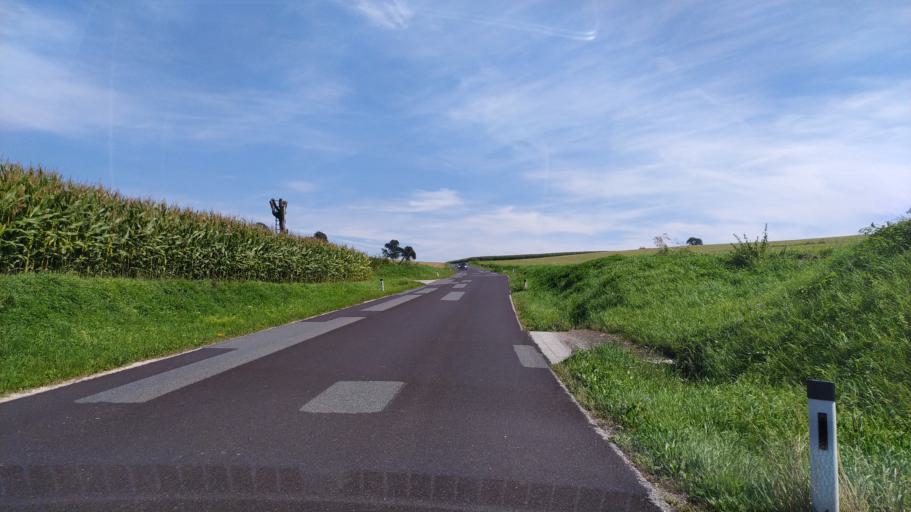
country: AT
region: Lower Austria
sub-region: Politischer Bezirk Amstetten
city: Wolfsbach
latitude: 48.1131
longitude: 14.7016
